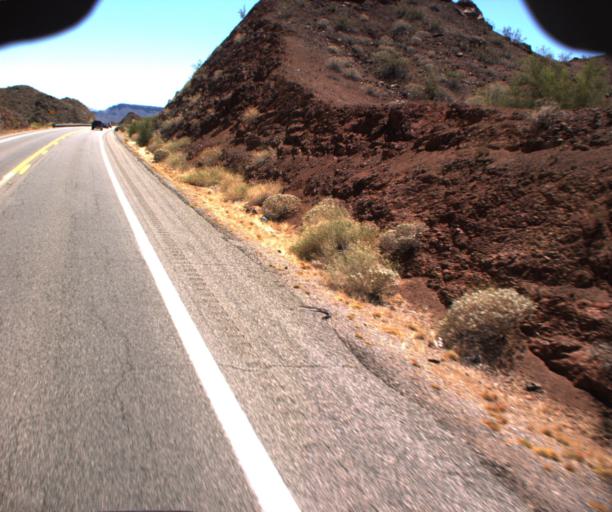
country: US
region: Arizona
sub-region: La Paz County
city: Cienega Springs
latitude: 34.3201
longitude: -114.1173
